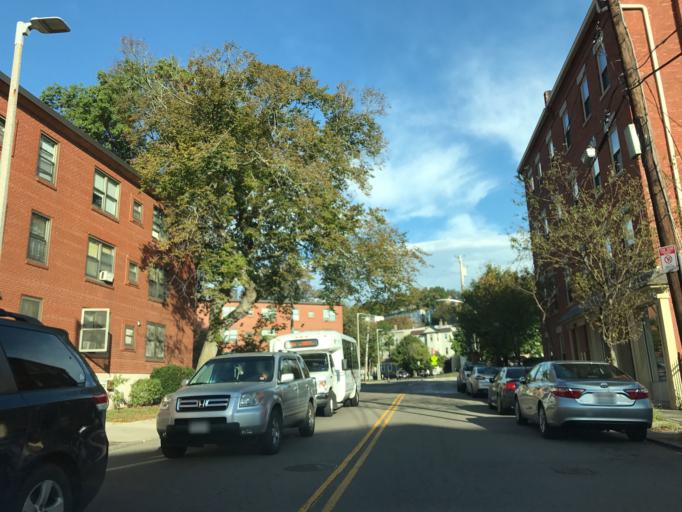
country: US
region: Massachusetts
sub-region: Norfolk County
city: Brookline
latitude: 42.3255
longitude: -71.0998
